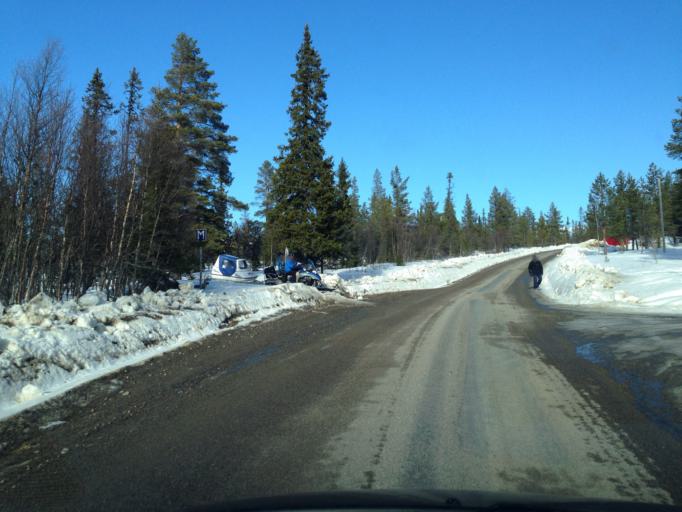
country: SE
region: Jaemtland
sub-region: Harjedalens Kommun
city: Sveg
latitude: 62.1310
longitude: 13.2643
